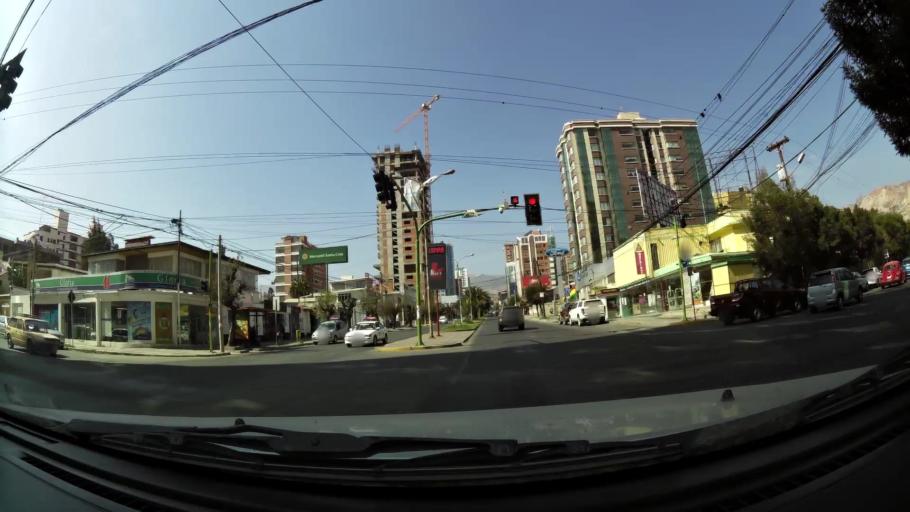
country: BO
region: La Paz
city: La Paz
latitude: -16.5408
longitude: -68.0895
